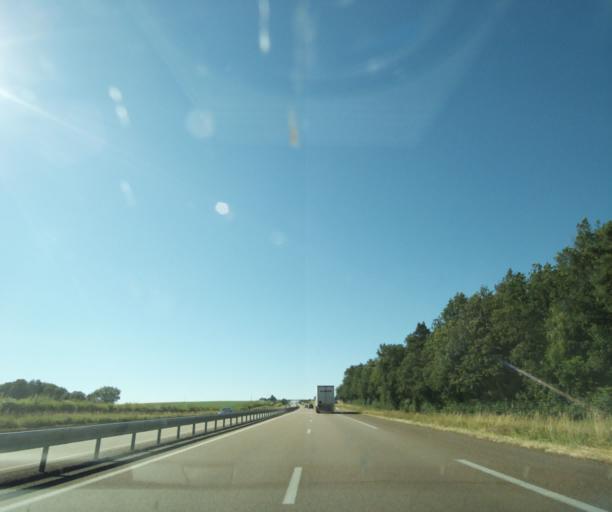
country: FR
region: Champagne-Ardenne
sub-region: Departement de la Haute-Marne
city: Chamarandes-Choignes
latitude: 47.9836
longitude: 5.1304
